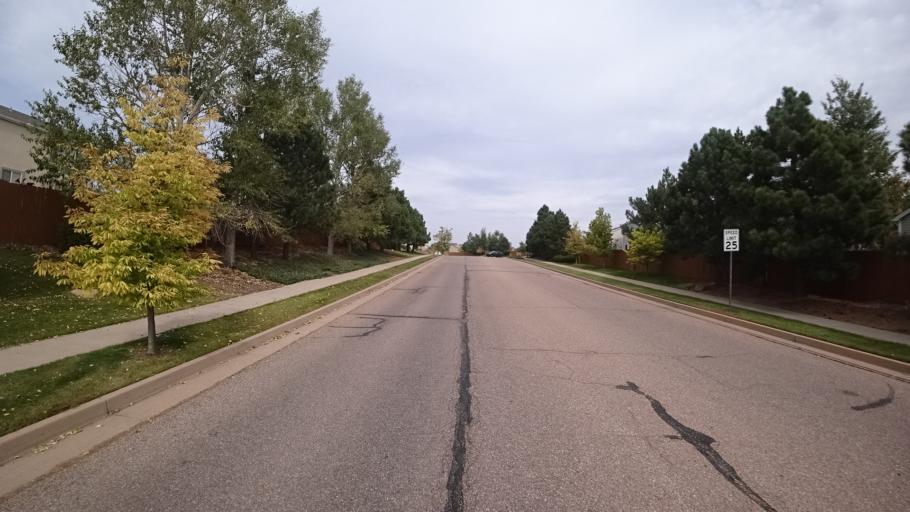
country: US
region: Colorado
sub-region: El Paso County
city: Cimarron Hills
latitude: 38.9122
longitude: -104.7056
